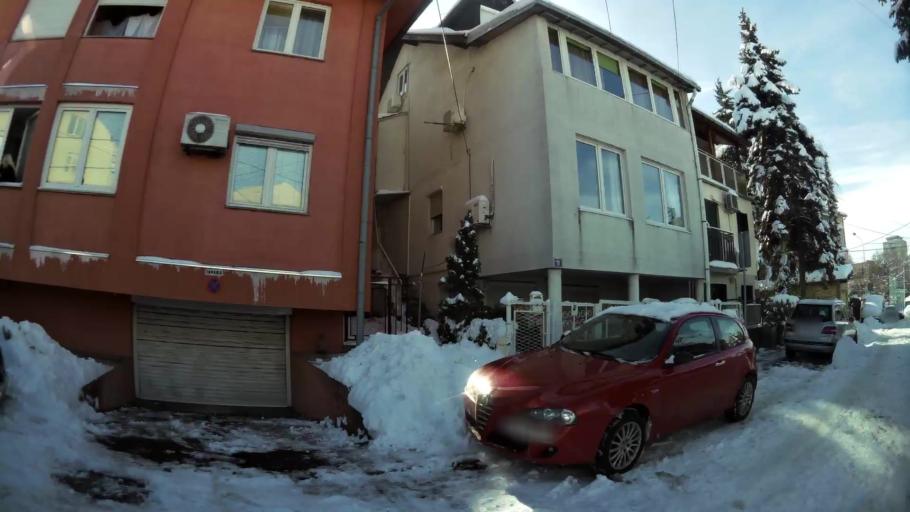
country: RS
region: Central Serbia
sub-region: Belgrade
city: Palilula
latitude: 44.7876
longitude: 20.5094
